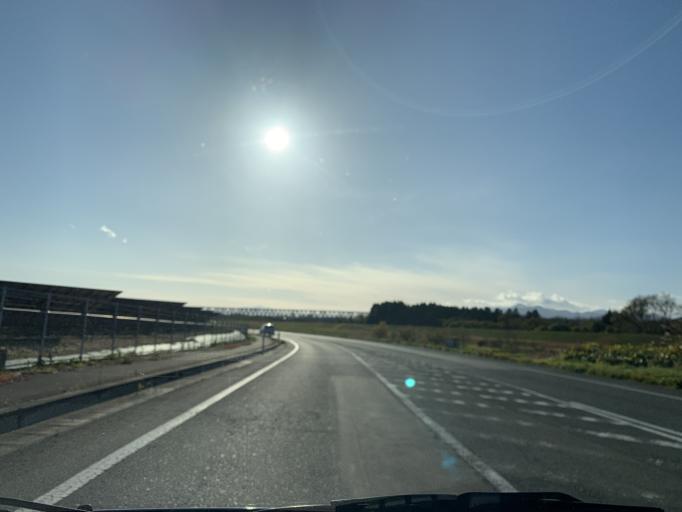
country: JP
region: Iwate
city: Kitakami
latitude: 39.2491
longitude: 141.1190
